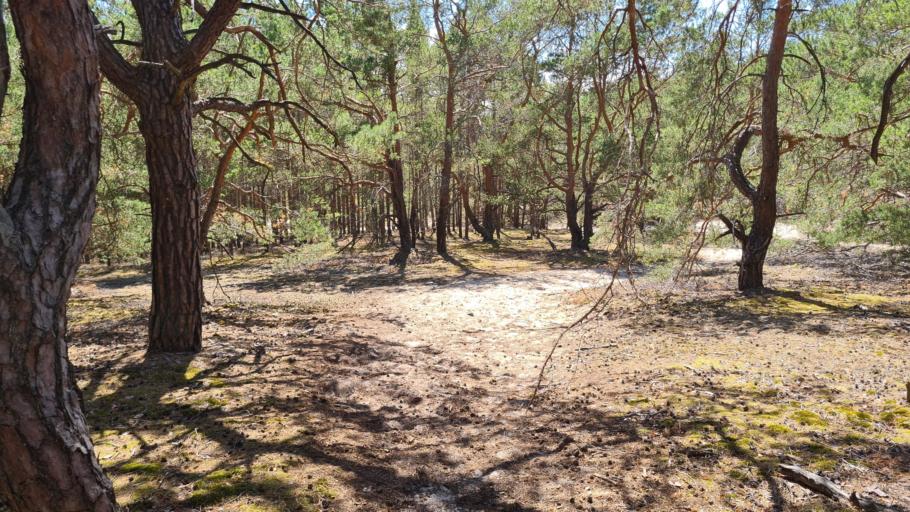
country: DE
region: Brandenburg
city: Trebbin
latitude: 52.2480
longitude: 13.1682
